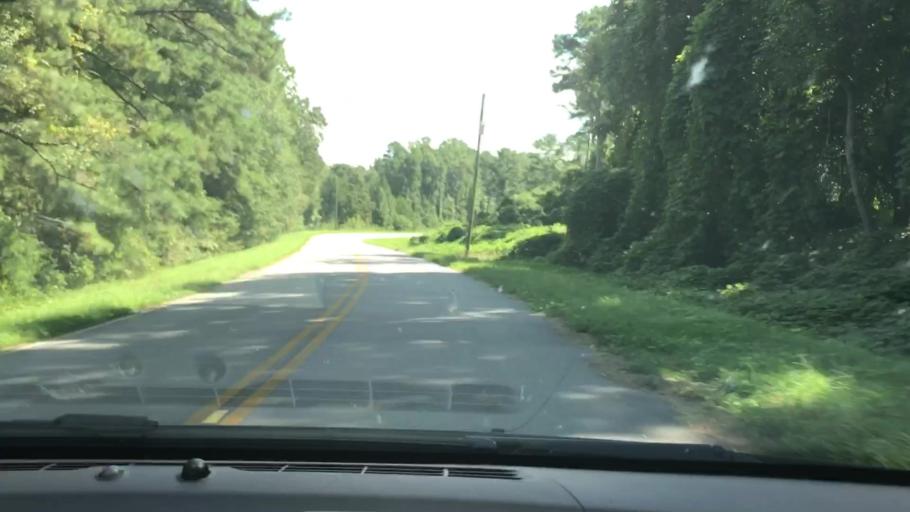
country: US
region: Georgia
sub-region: Troup County
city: La Grange
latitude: 33.0759
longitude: -85.1304
